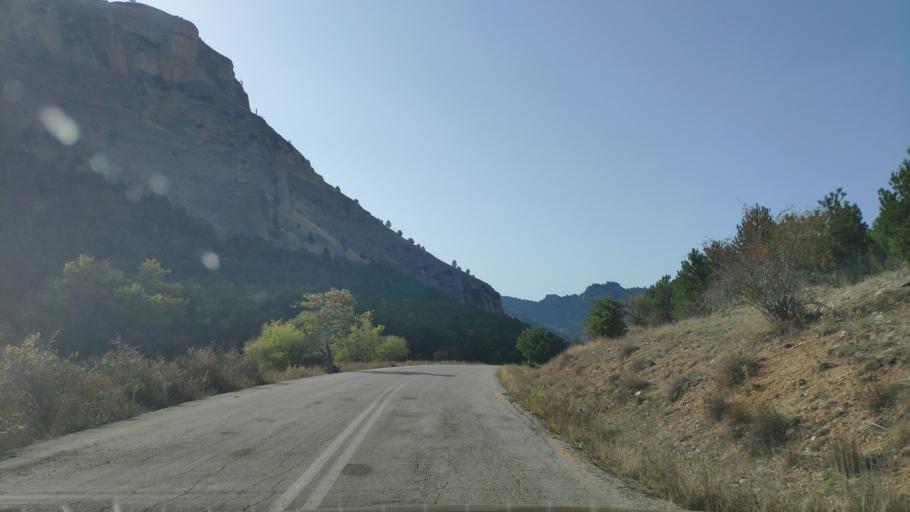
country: GR
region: West Greece
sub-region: Nomos Achaias
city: Aiyira
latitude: 38.0399
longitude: 22.3956
